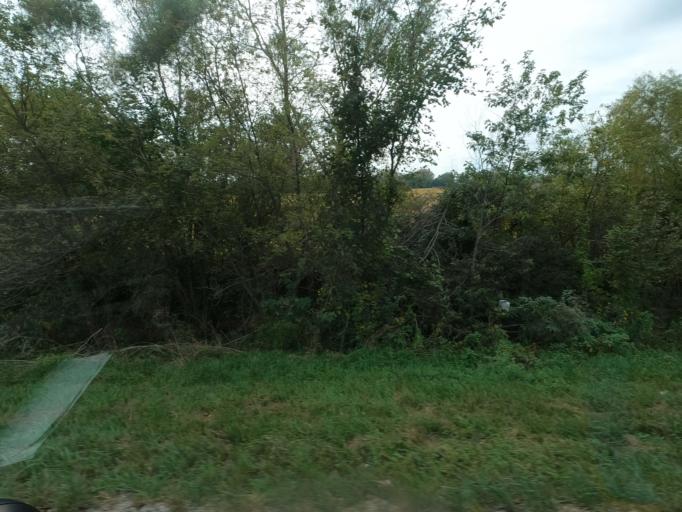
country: US
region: Iowa
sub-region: Jefferson County
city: Fairfield
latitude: 40.8788
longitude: -92.1575
